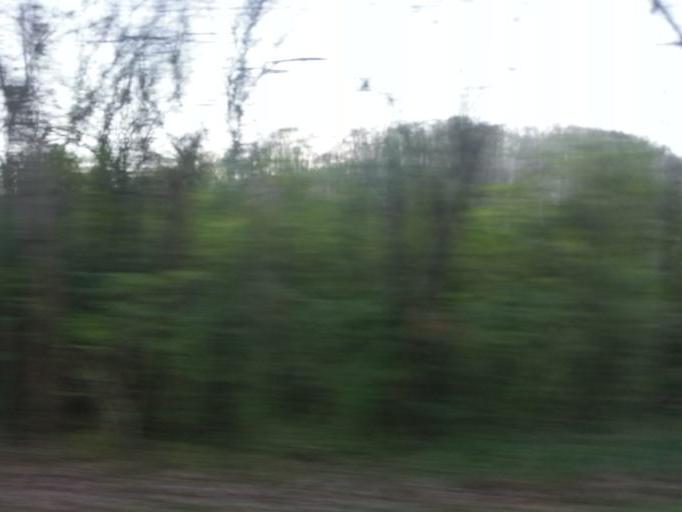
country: US
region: Tennessee
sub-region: Anderson County
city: Norris
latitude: 36.2136
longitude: -84.0742
